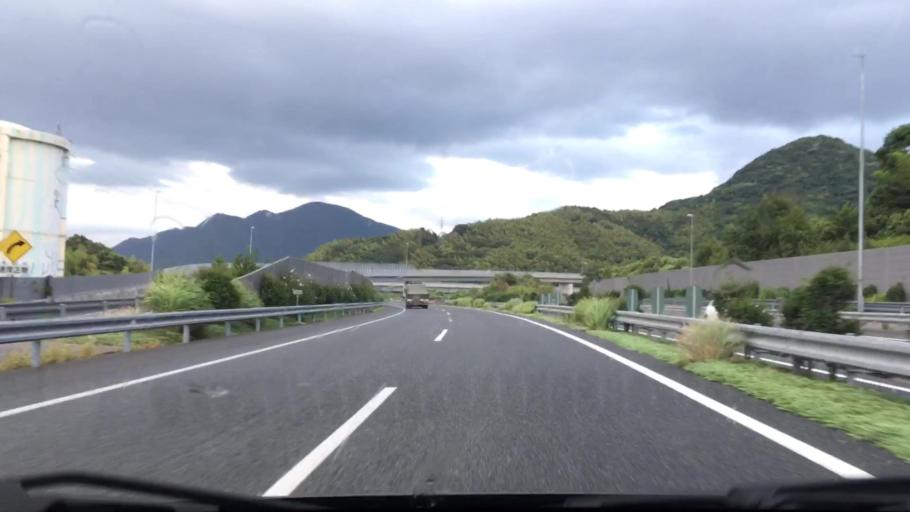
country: JP
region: Fukuoka
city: Kitakyushu
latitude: 33.8132
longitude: 130.8827
